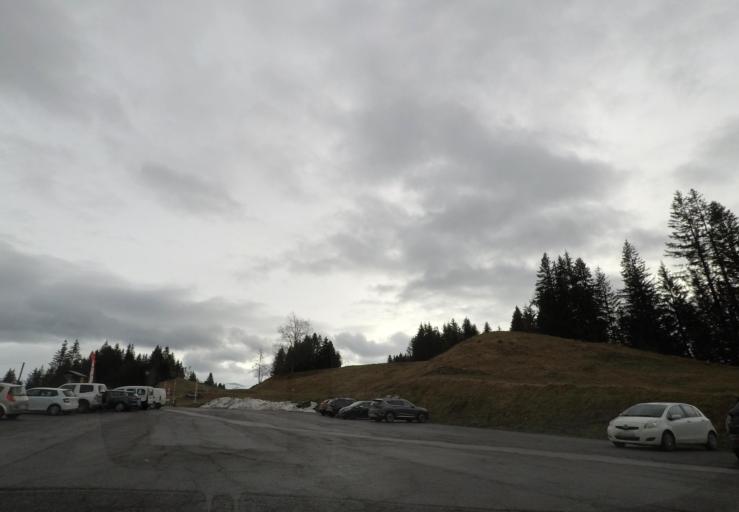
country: FR
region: Rhone-Alpes
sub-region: Departement de la Haute-Savoie
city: Chatillon-sur-Cluses
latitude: 46.0788
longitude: 6.6216
